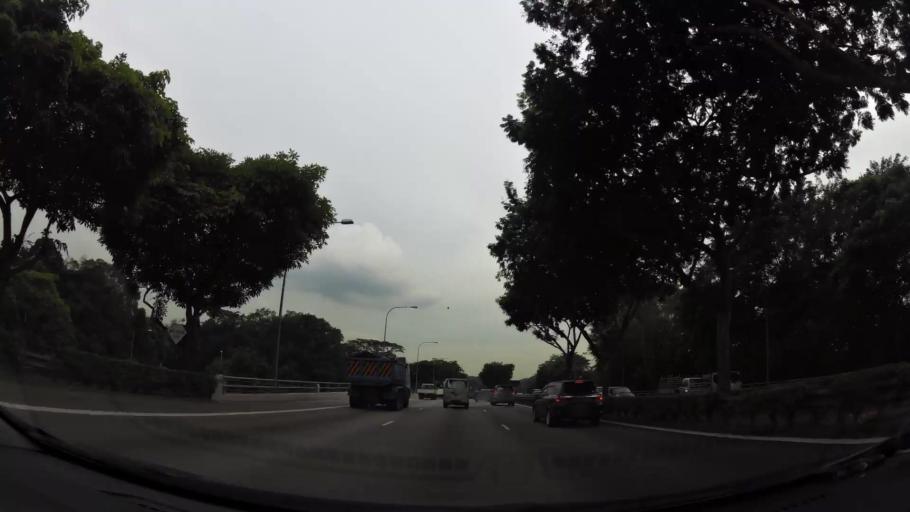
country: MY
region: Johor
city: Johor Bahru
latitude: 1.4026
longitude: 103.8119
